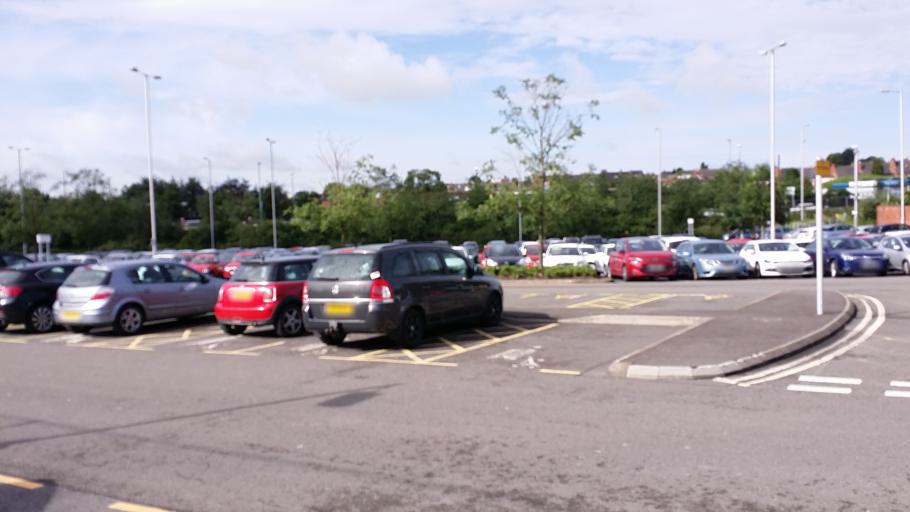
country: GB
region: England
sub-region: Nottinghamshire
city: Hucknall
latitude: 53.0382
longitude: -1.1959
